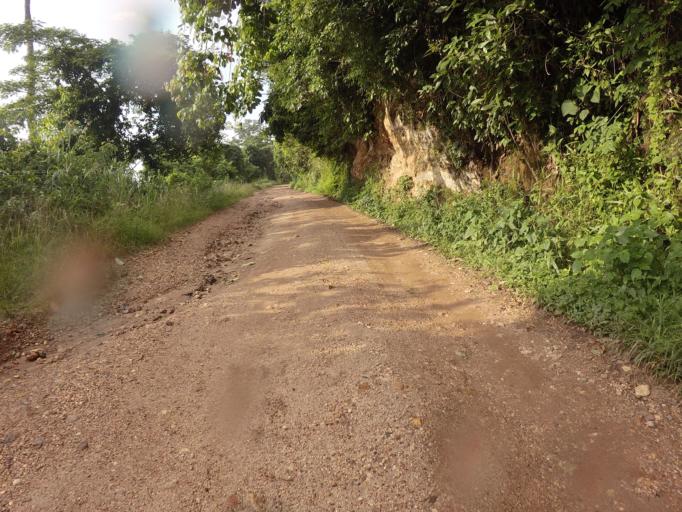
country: GH
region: Volta
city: Kpandu
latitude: 6.8411
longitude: 0.4306
